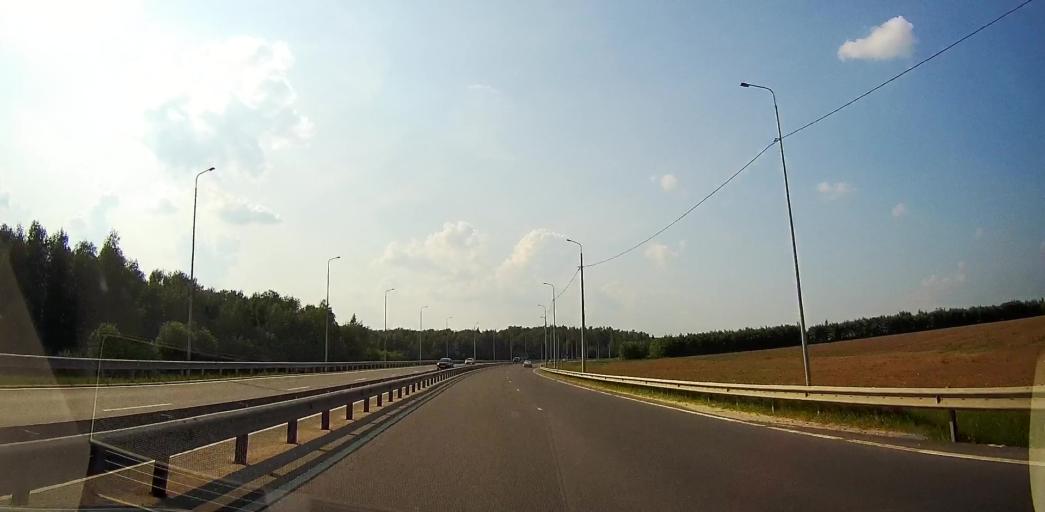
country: RU
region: Moskovskaya
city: Vostryakovo
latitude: 55.4175
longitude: 37.8529
